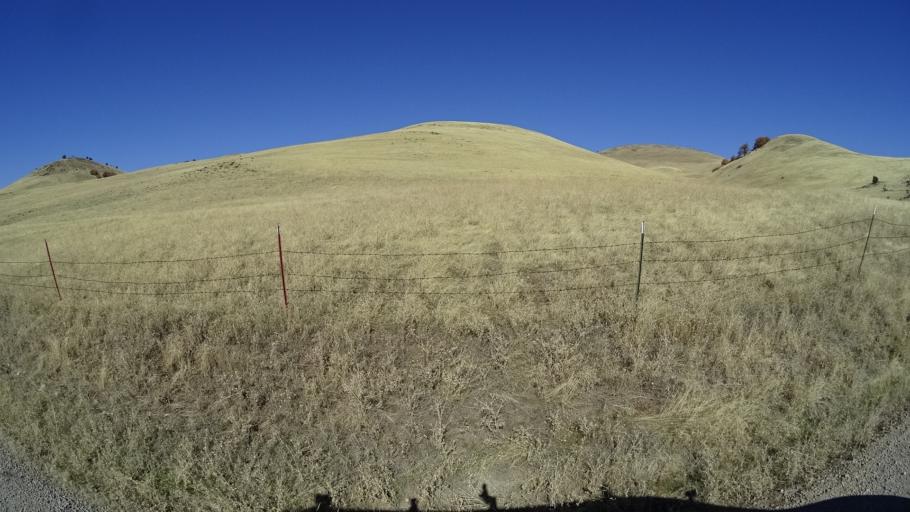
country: US
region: California
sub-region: Siskiyou County
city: Montague
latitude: 41.7934
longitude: -122.3474
